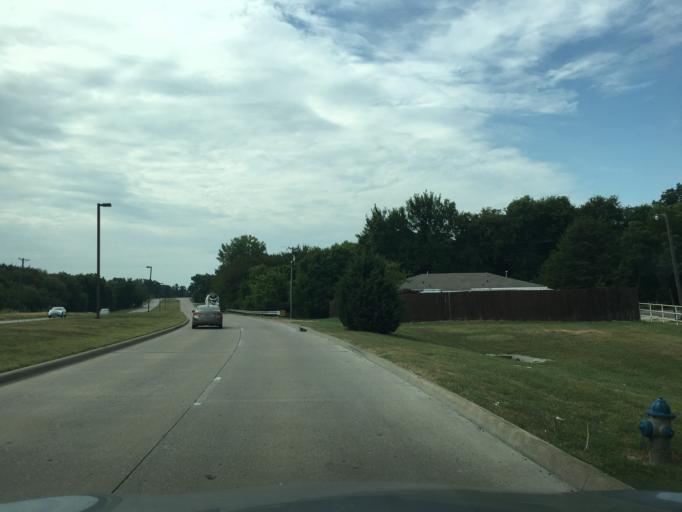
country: US
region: Texas
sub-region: Collin County
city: McKinney
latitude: 33.1995
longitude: -96.5998
